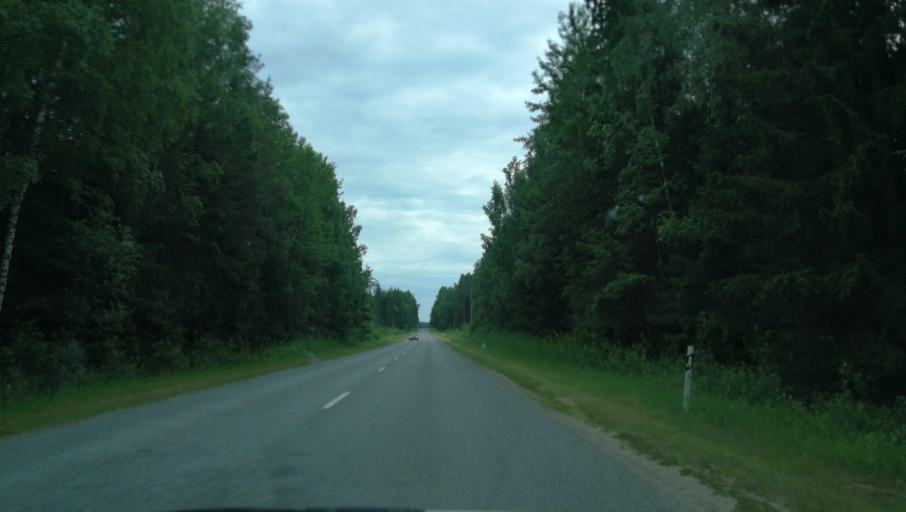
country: LV
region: Valmieras Rajons
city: Valmiera
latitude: 57.7027
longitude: 25.4271
